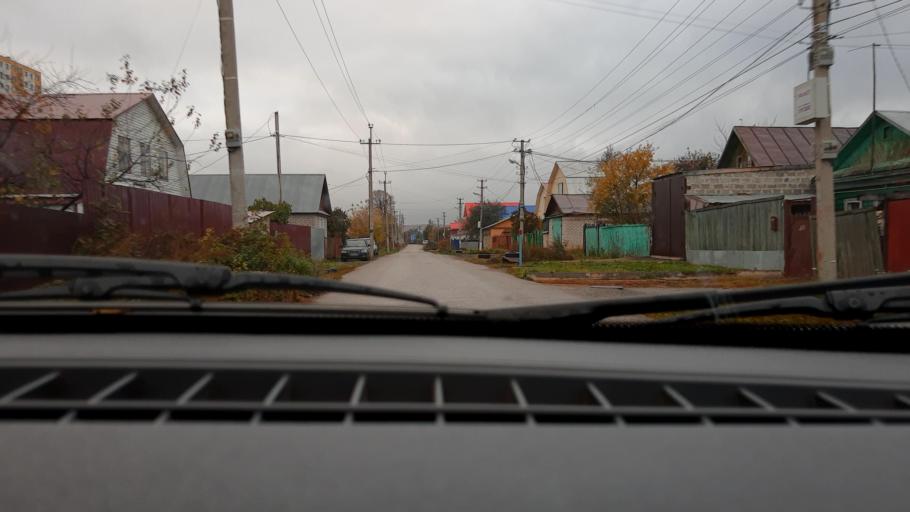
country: RU
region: Bashkortostan
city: Mikhaylovka
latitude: 54.7896
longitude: 55.8876
